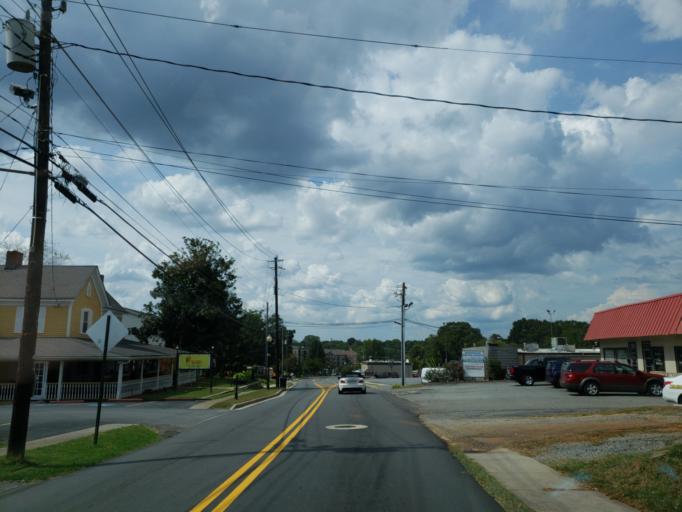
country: US
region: Georgia
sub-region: Cobb County
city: Kennesaw
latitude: 34.0190
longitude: -84.6134
